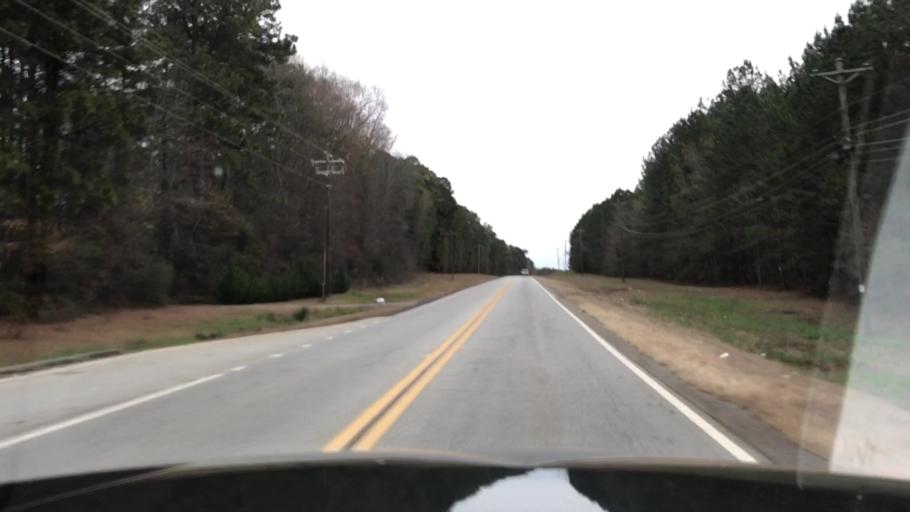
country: US
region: Georgia
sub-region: Walton County
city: Monroe
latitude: 33.7983
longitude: -83.6643
